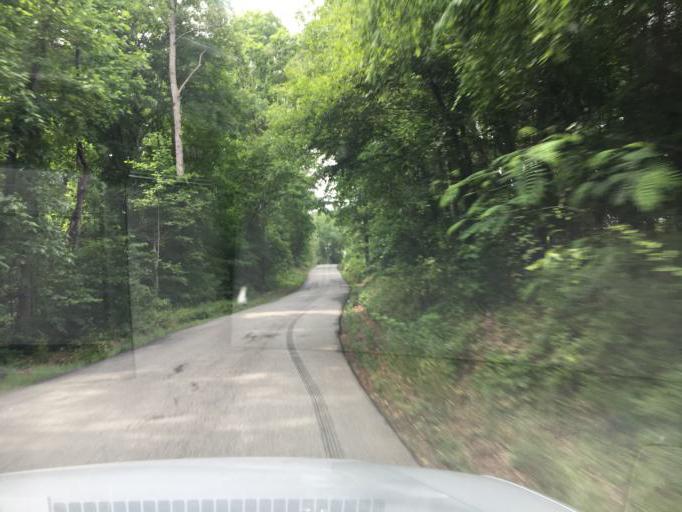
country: US
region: South Carolina
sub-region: Spartanburg County
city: Fairforest
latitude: 34.9068
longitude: -82.0364
